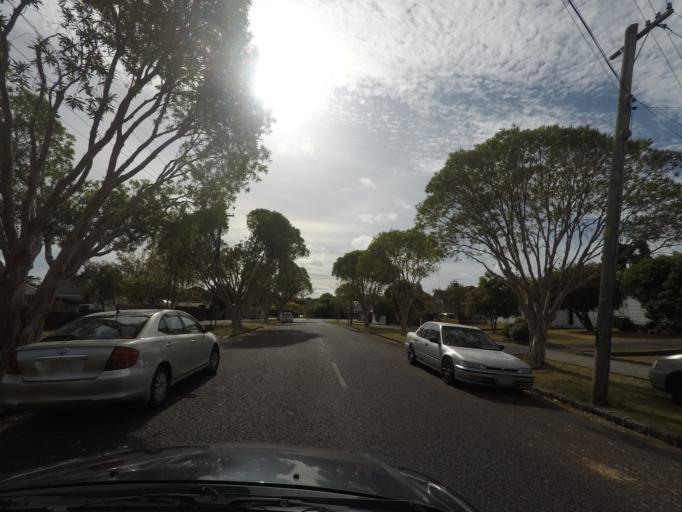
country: NZ
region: Auckland
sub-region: Auckland
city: Rosebank
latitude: -36.8777
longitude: 174.7151
